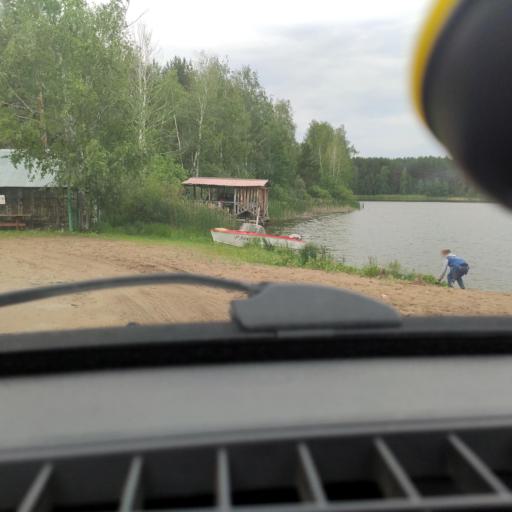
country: RU
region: Samara
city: Zhigulevsk
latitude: 53.5039
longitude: 49.5021
